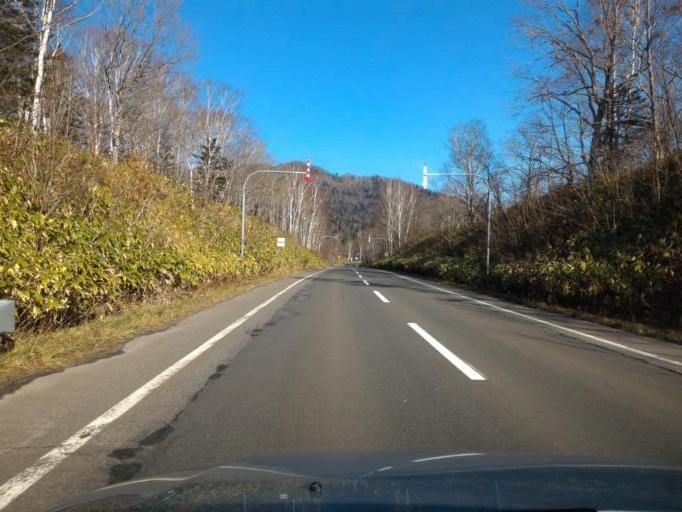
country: JP
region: Hokkaido
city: Ashibetsu
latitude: 43.2999
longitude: 142.1130
